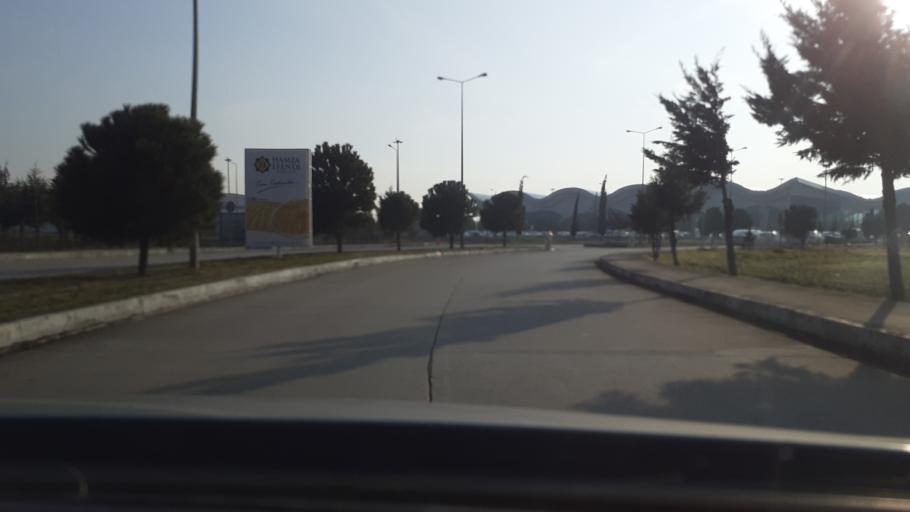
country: TR
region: Hatay
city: Serinyol
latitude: 36.3645
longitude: 36.2787
